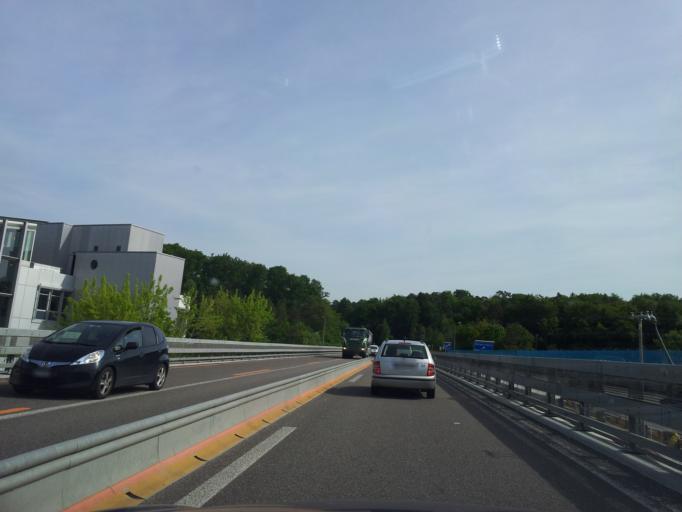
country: CH
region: Zurich
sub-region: Bezirk Buelach
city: Buelach / Soligaenter
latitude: 47.5283
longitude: 8.5323
